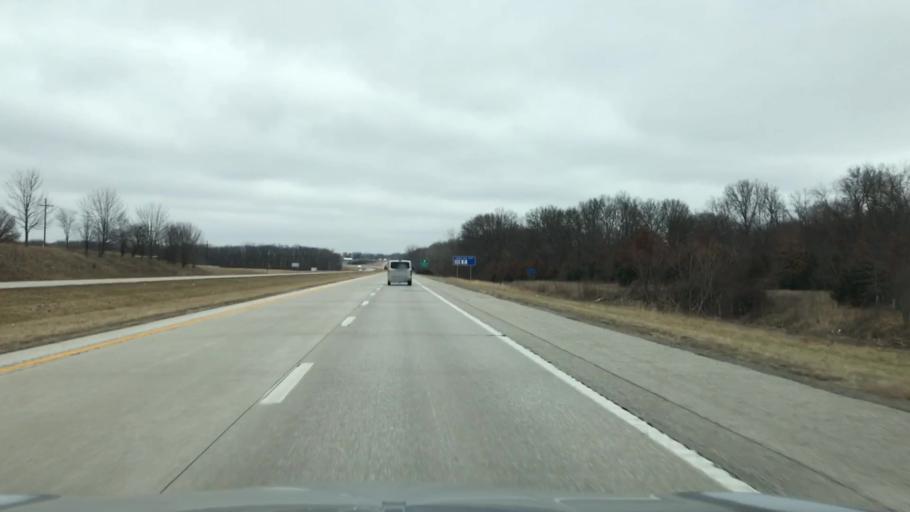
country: US
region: Missouri
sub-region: Linn County
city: Brookfield
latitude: 39.7764
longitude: -93.0925
